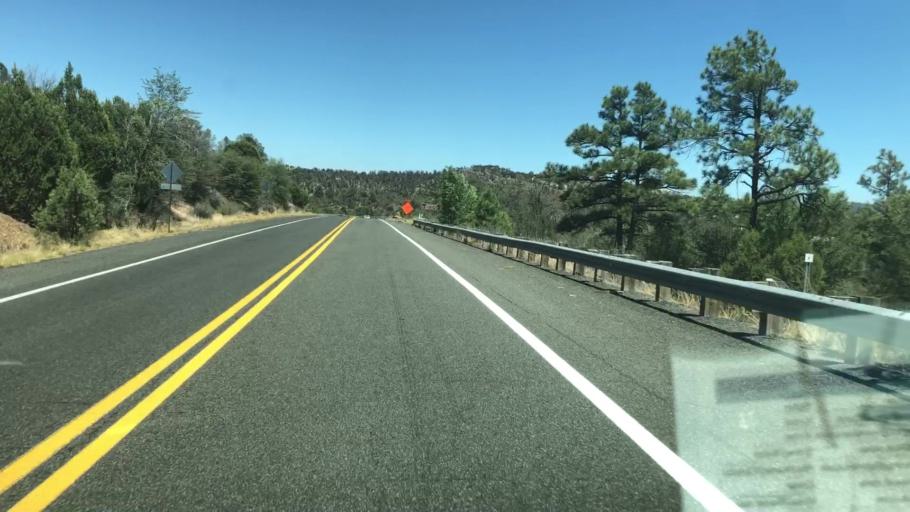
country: US
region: Arizona
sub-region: Yavapai County
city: Prescott
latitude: 34.5782
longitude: -112.5270
